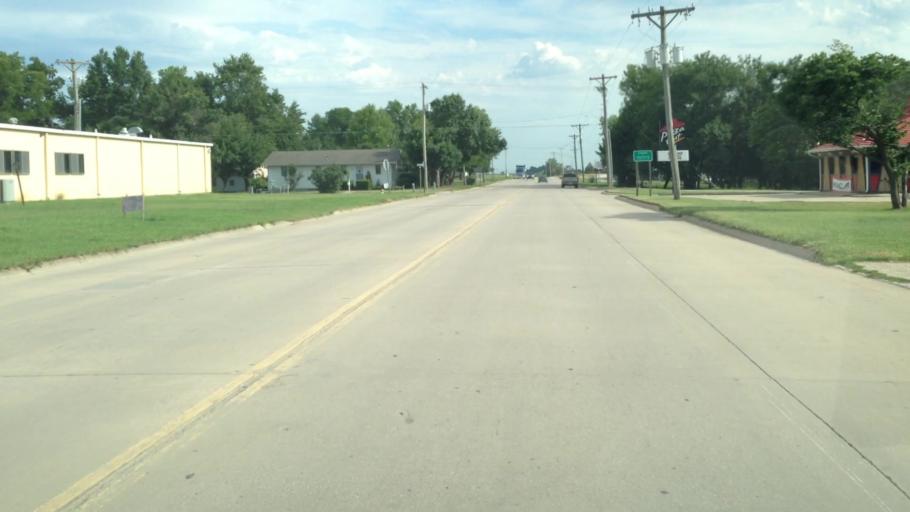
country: US
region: Kansas
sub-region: Woodson County
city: Yates Center
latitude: 37.8771
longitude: -95.7389
